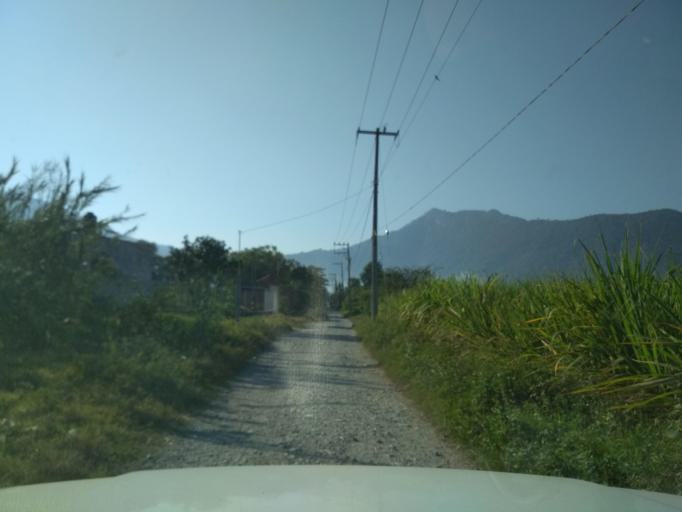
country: MX
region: Veracruz
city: Jalapilla
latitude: 18.8273
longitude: -97.0795
